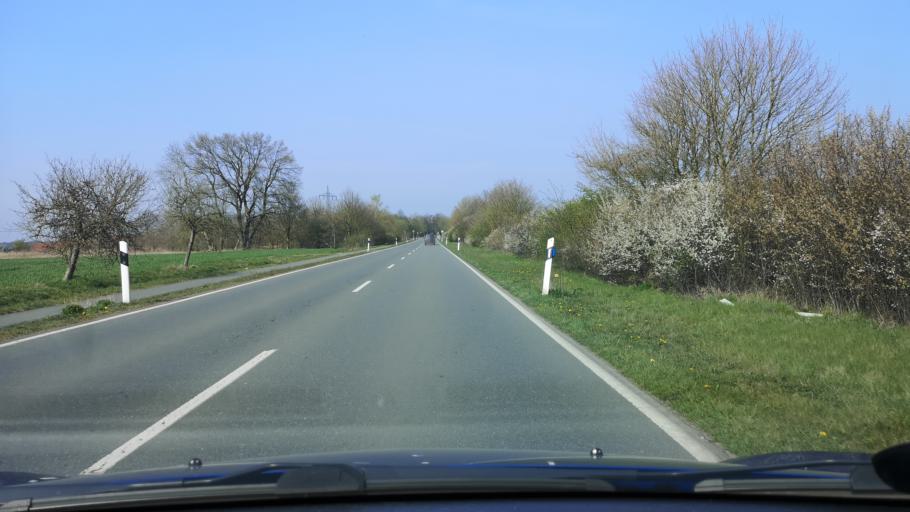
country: DE
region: Lower Saxony
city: Neustadt am Rubenberge
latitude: 52.5191
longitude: 9.4764
